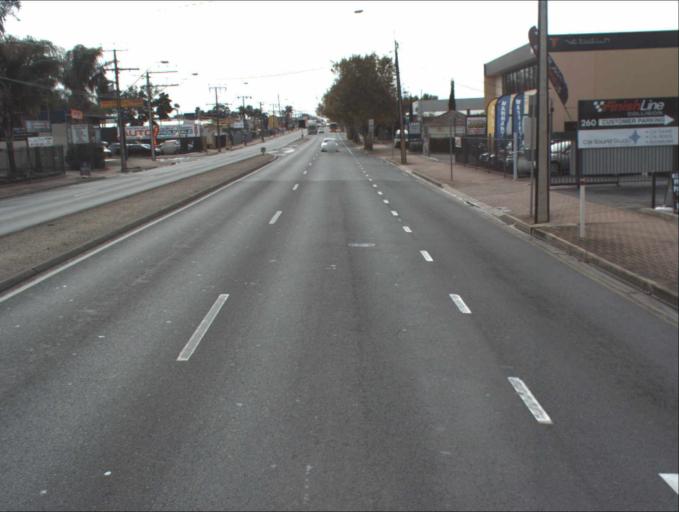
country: AU
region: South Australia
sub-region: Port Adelaide Enfield
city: Klemzig
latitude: -34.8741
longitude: 138.6334
